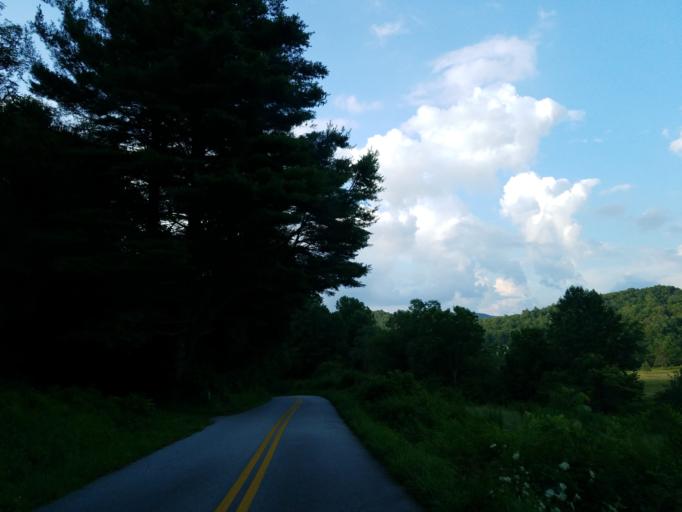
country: US
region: Georgia
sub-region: Lumpkin County
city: Dahlonega
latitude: 34.6901
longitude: -84.0796
